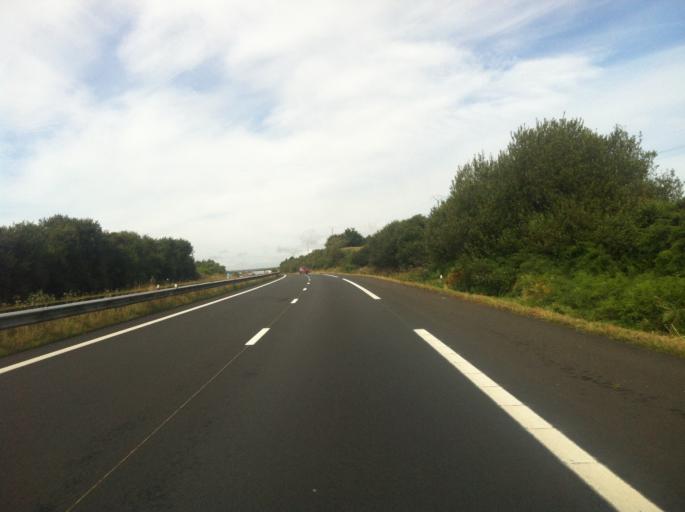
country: FR
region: Brittany
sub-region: Departement du Finistere
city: Guerlesquin
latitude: 48.5640
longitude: -3.5279
